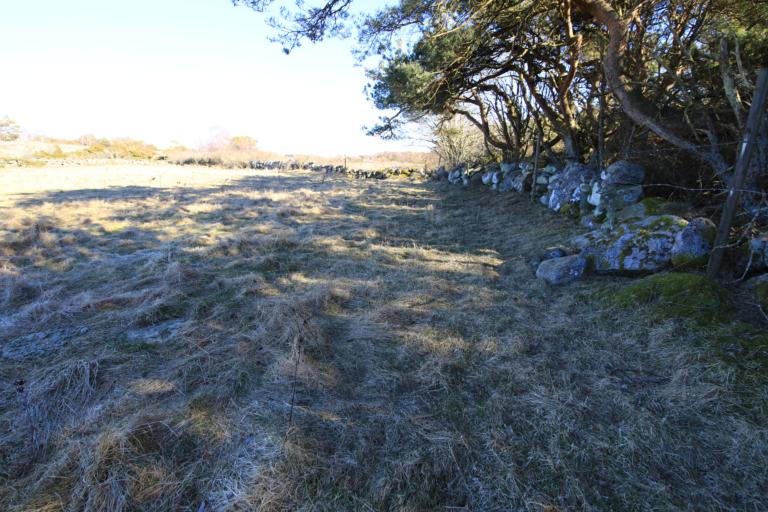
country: SE
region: Halland
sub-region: Kungsbacka Kommun
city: Frillesas
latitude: 57.2253
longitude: 12.1288
